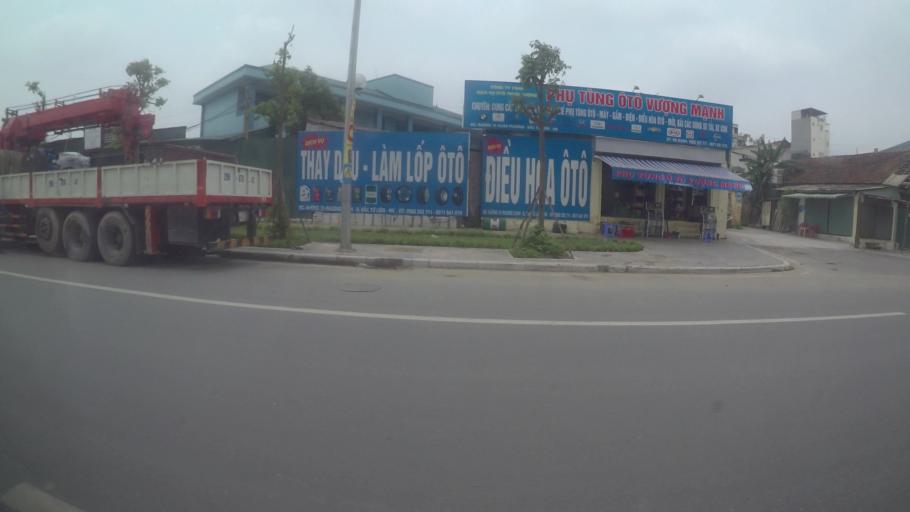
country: VN
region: Ha Noi
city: Cau Dien
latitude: 21.0482
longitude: 105.7356
